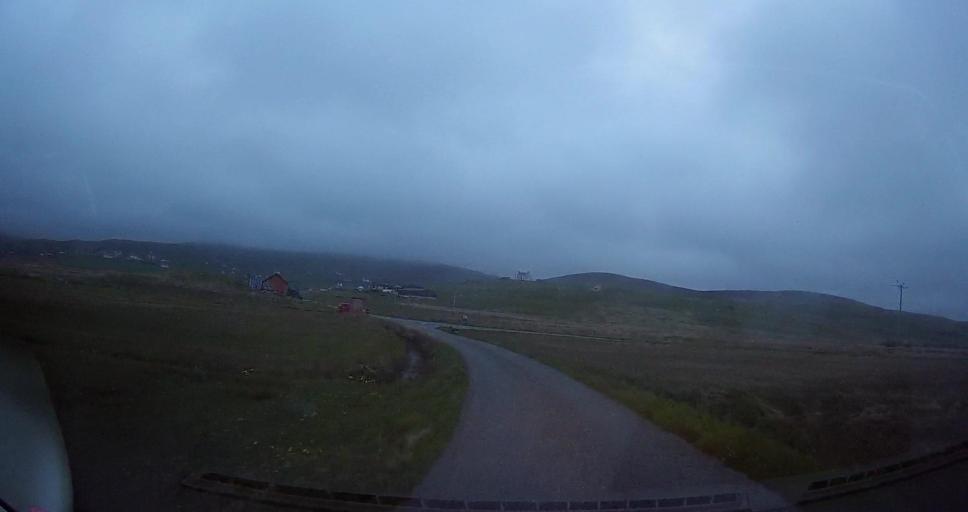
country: GB
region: Scotland
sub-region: Shetland Islands
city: Sandwick
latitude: 60.0463
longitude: -1.2070
